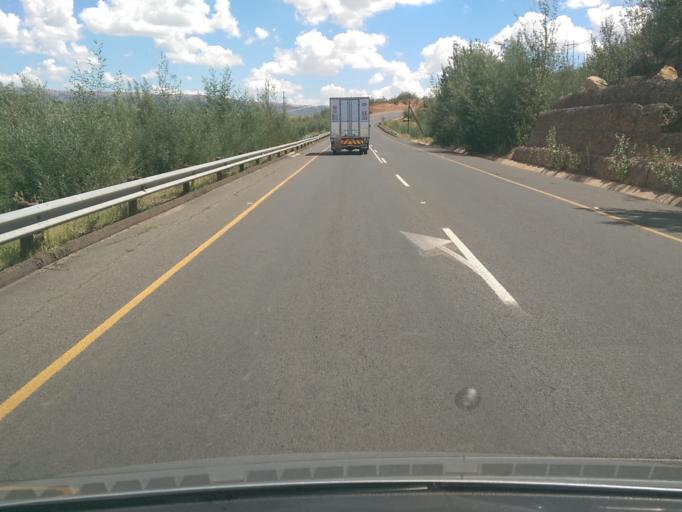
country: LS
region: Maseru
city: Maseru
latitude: -29.3993
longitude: 27.5333
